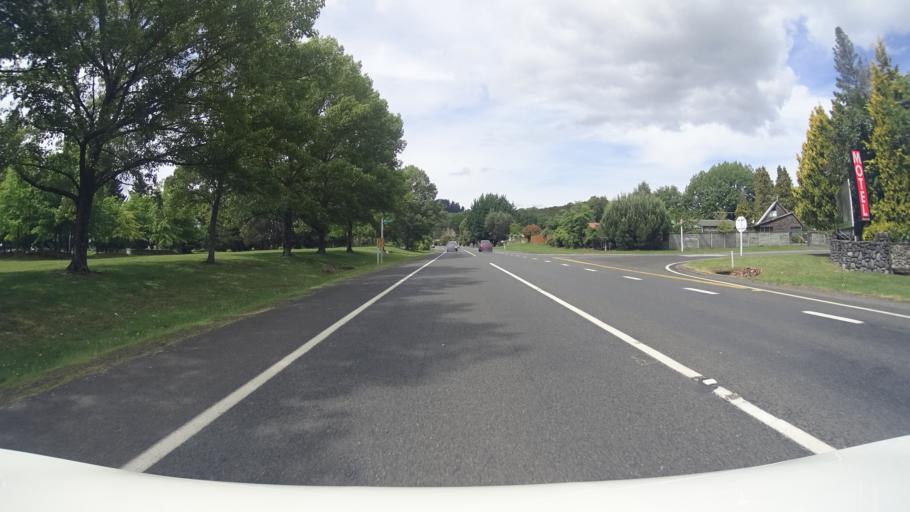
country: NZ
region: Waikato
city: Turangi
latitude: -38.9888
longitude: 175.8147
